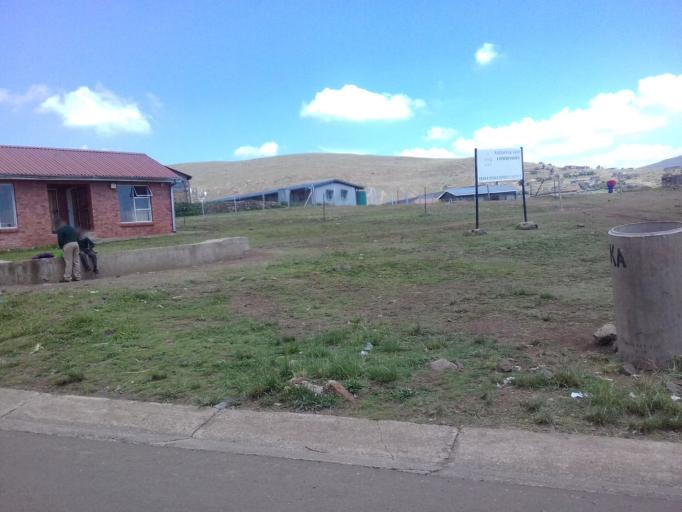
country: LS
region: Thaba-Tseka
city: Thaba-Tseka
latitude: -29.5226
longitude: 28.6089
